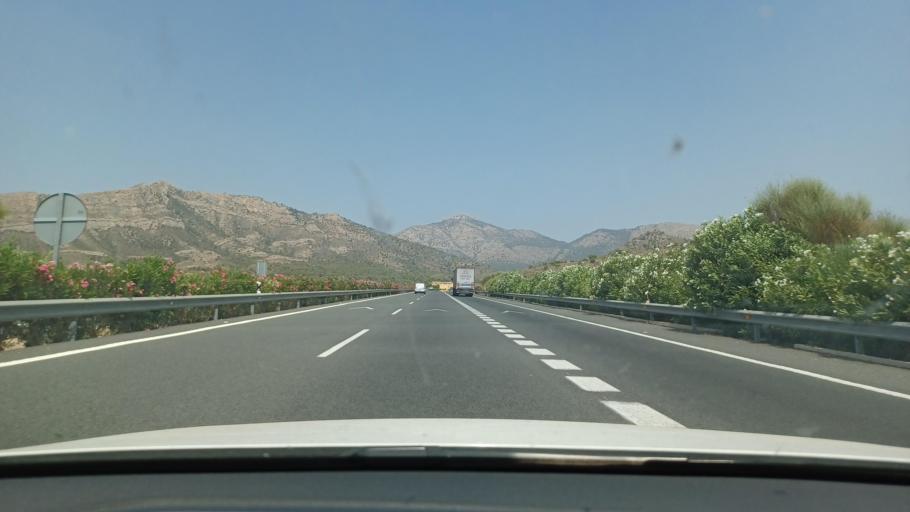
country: ES
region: Valencia
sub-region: Provincia de Alicante
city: Agost
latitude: 38.4687
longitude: -0.5872
